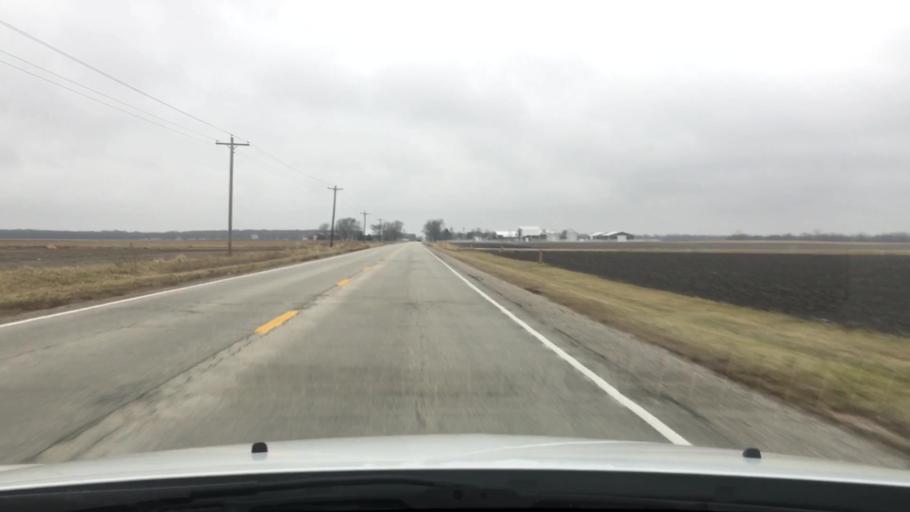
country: US
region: Illinois
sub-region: Iroquois County
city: Watseka
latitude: 40.8869
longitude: -87.8035
